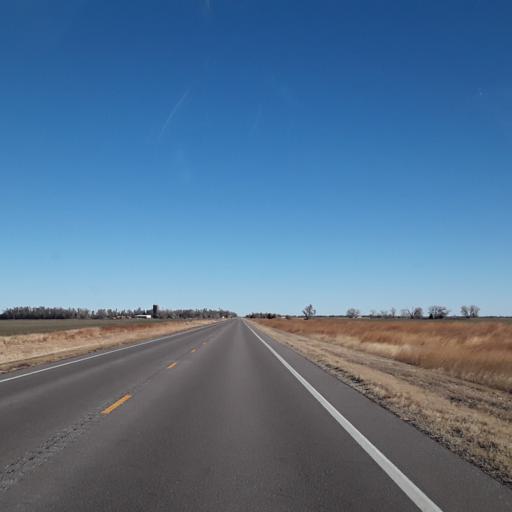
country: US
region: Kansas
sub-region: Pawnee County
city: Larned
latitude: 38.1093
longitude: -99.1946
